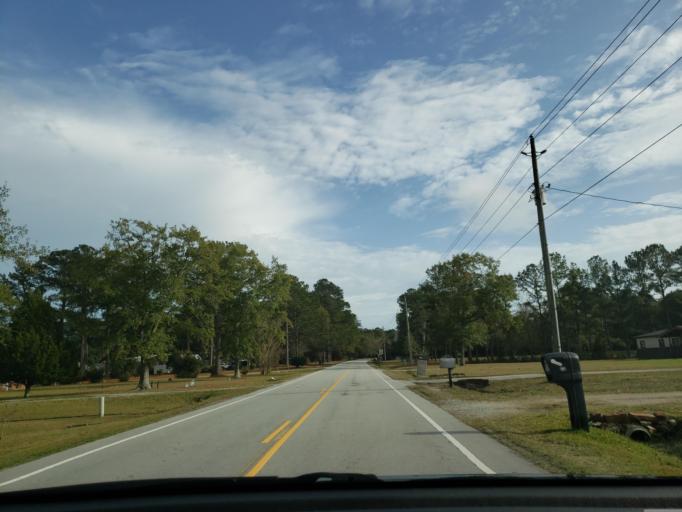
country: US
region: North Carolina
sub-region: Onslow County
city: Jacksonville
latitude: 34.6589
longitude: -77.4801
